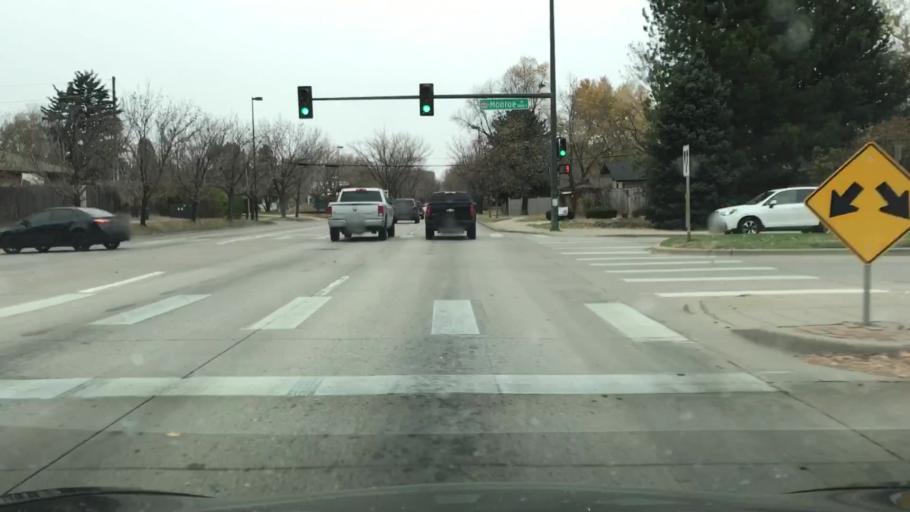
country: US
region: Colorado
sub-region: Arapahoe County
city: Glendale
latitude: 39.6786
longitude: -104.9450
